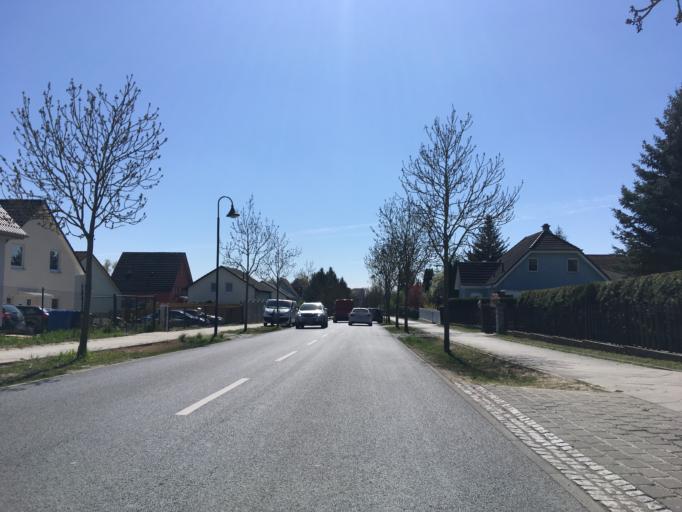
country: DE
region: Brandenburg
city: Bernau bei Berlin
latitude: 52.6774
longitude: 13.5546
